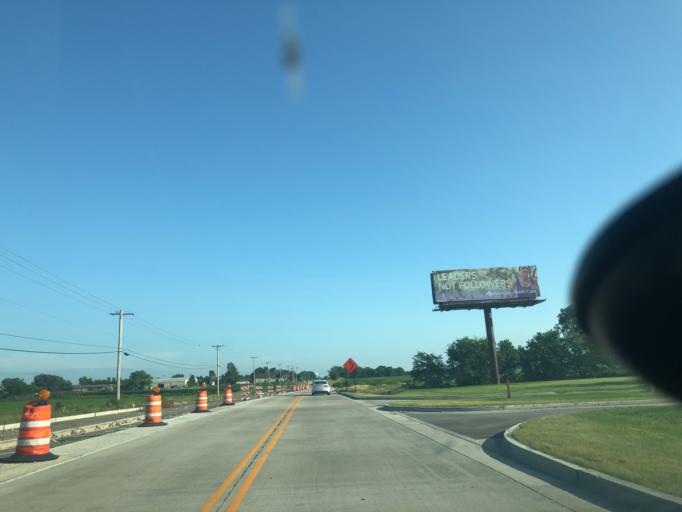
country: US
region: Illinois
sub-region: Will County
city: Homer Glen
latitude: 41.5987
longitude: -87.8915
